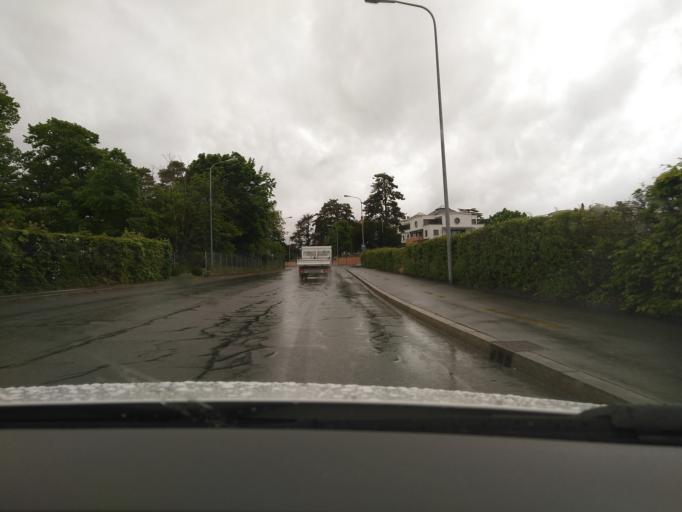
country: CH
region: Vaud
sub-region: Nyon District
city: Nyon
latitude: 46.3794
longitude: 6.2338
